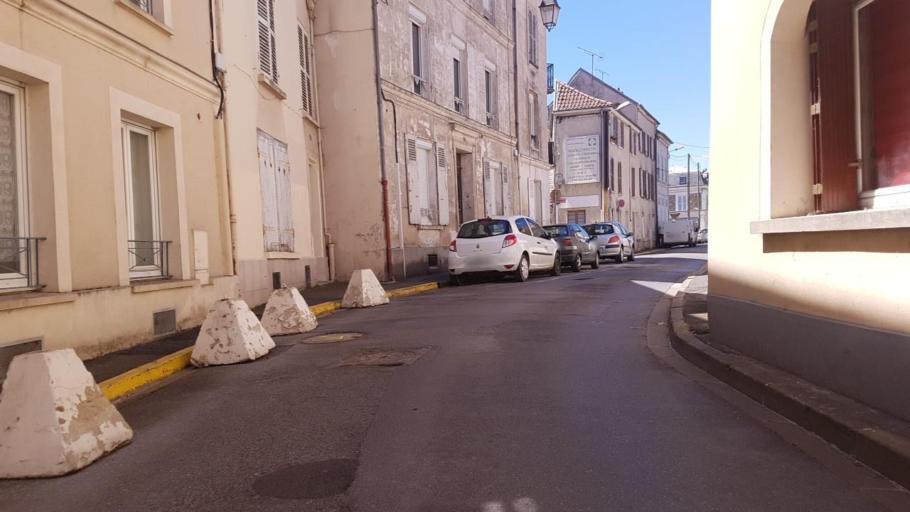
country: FR
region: Ile-de-France
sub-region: Departement de Seine-et-Marne
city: La Ferte-sous-Jouarre
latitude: 48.9489
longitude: 3.1296
